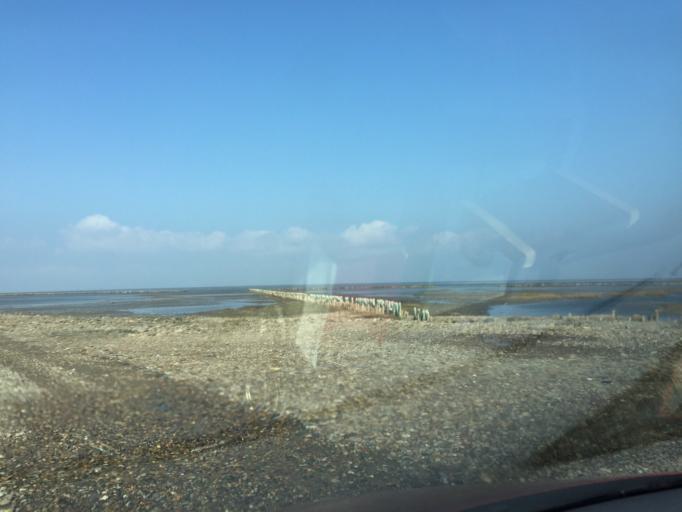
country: DK
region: South Denmark
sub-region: Esbjerg Kommune
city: Ribe
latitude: 55.3098
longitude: 8.6430
